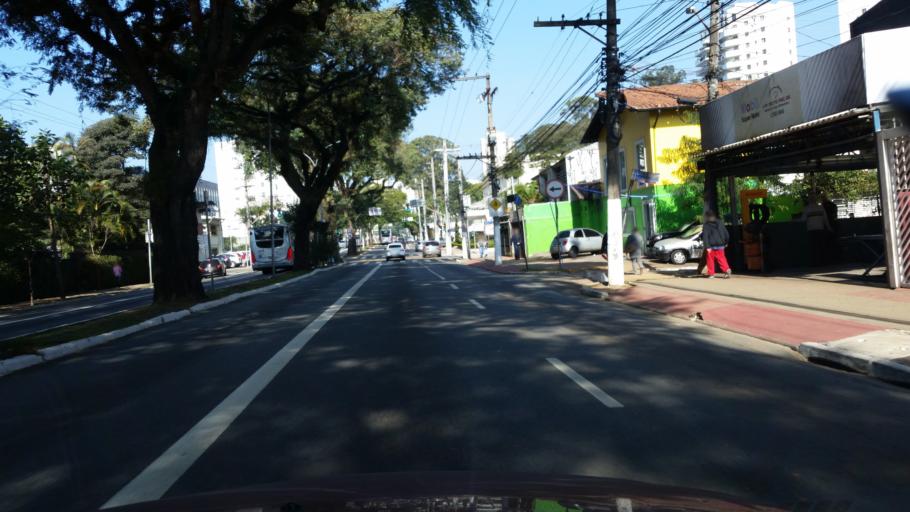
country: BR
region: Sao Paulo
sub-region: Diadema
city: Diadema
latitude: -23.6377
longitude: -46.6968
